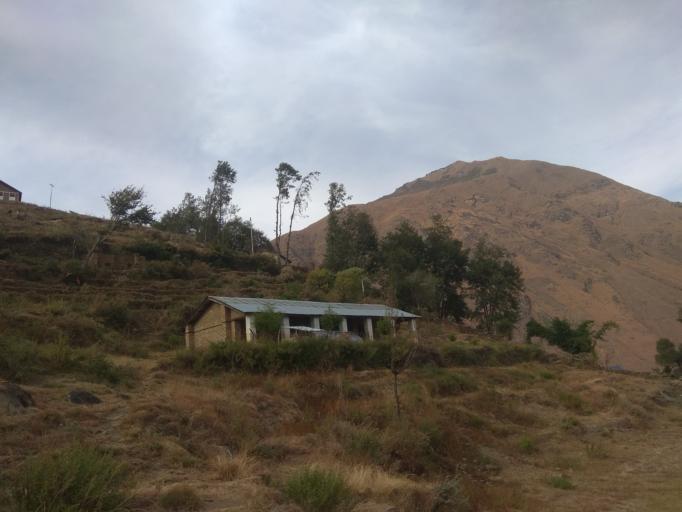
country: NP
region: Mid Western
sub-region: Bheri Zone
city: Dailekh
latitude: 29.2505
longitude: 81.6691
